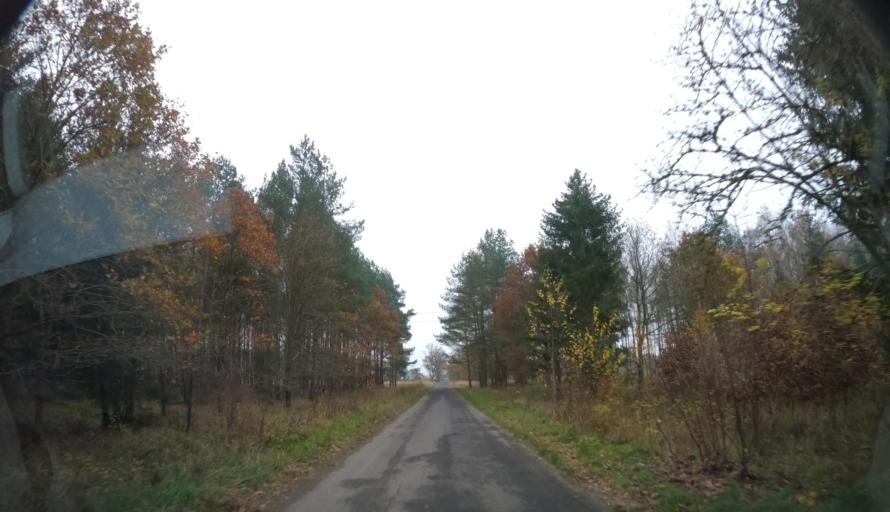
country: PL
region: West Pomeranian Voivodeship
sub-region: Powiat lobeski
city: Radowo Male
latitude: 53.6819
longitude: 15.4639
